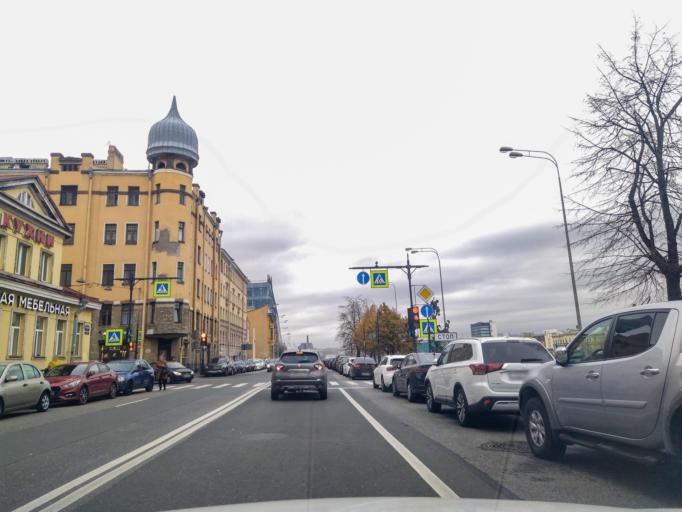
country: RU
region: St.-Petersburg
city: Petrogradka
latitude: 59.9605
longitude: 30.3348
